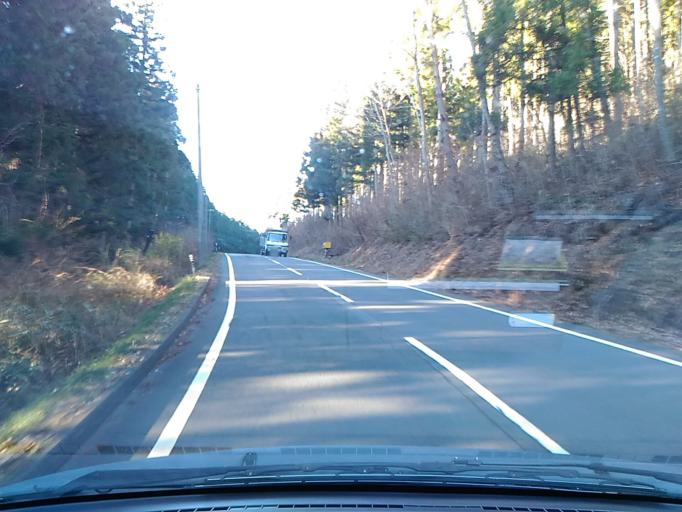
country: JP
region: Ibaraki
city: Kitaibaraki
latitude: 36.9524
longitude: 140.5829
